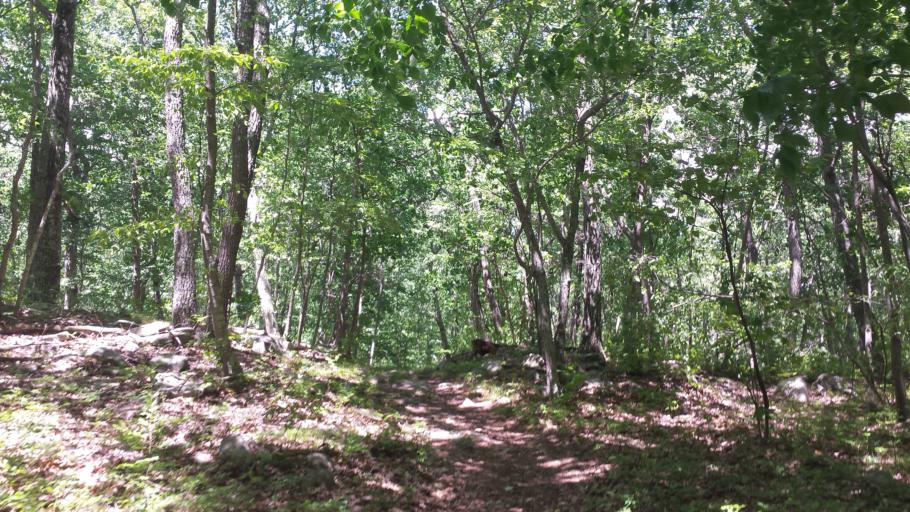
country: US
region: New York
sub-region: Westchester County
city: Pound Ridge
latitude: 41.2648
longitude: -73.5729
